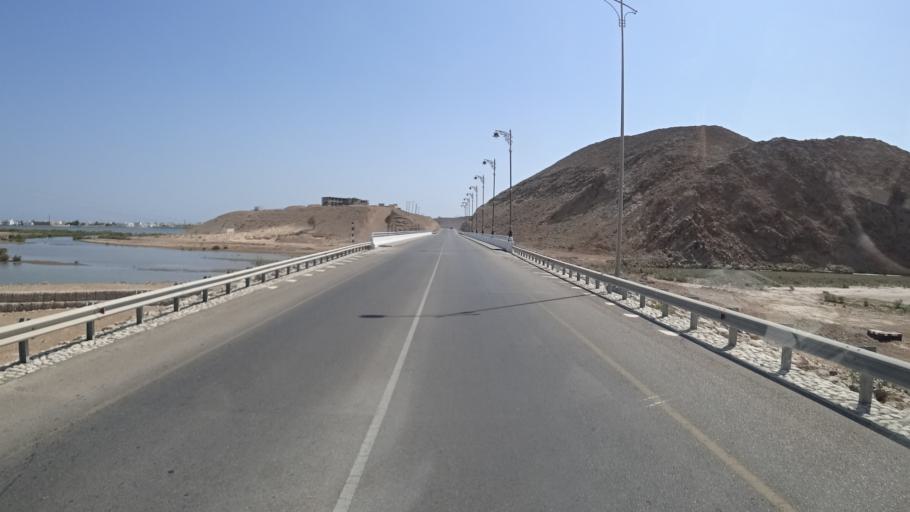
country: OM
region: Ash Sharqiyah
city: Sur
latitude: 22.5496
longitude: 59.5270
